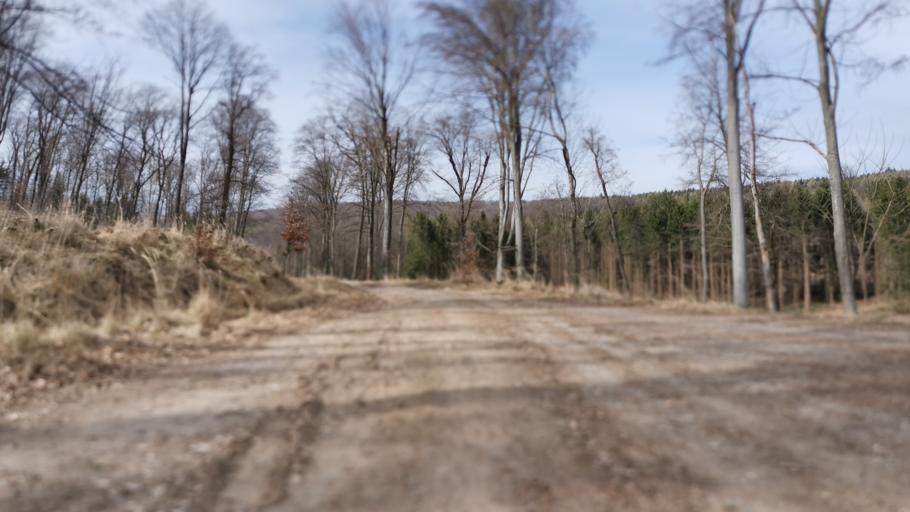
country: CZ
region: South Moravian
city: Knezdub
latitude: 48.8225
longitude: 17.3497
